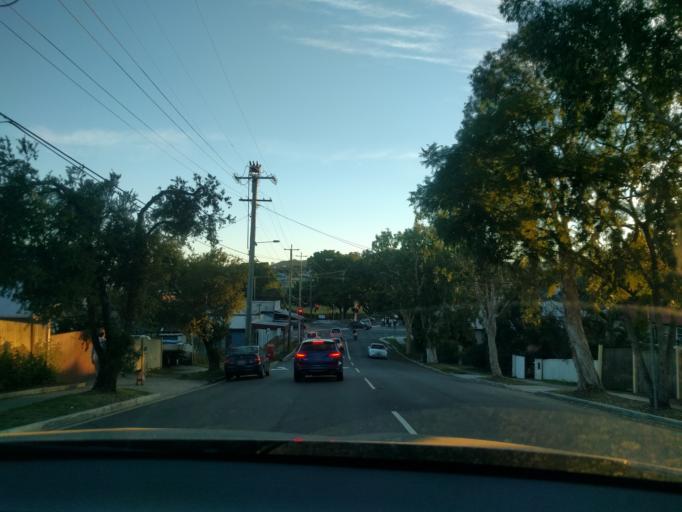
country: AU
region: Queensland
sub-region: Brisbane
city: Milton
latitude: -27.4663
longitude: 153.0021
